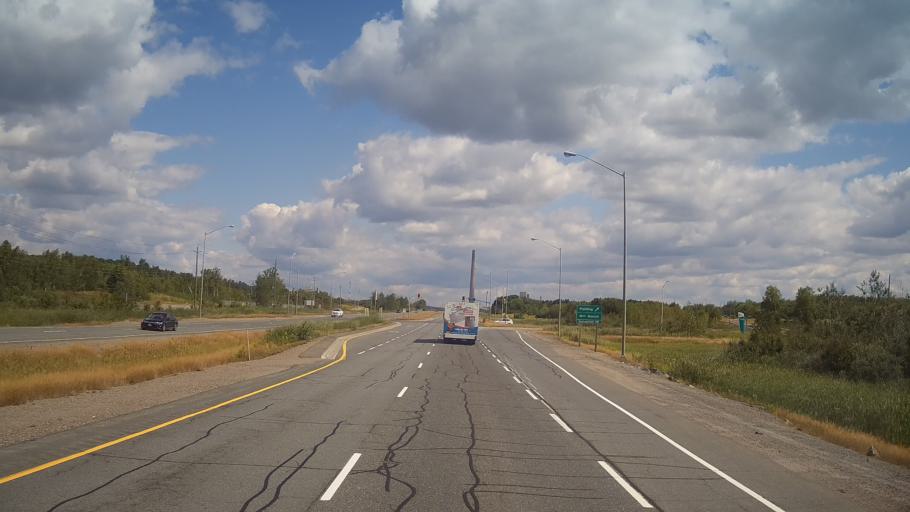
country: CA
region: Ontario
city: Greater Sudbury
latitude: 46.4470
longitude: -81.0976
